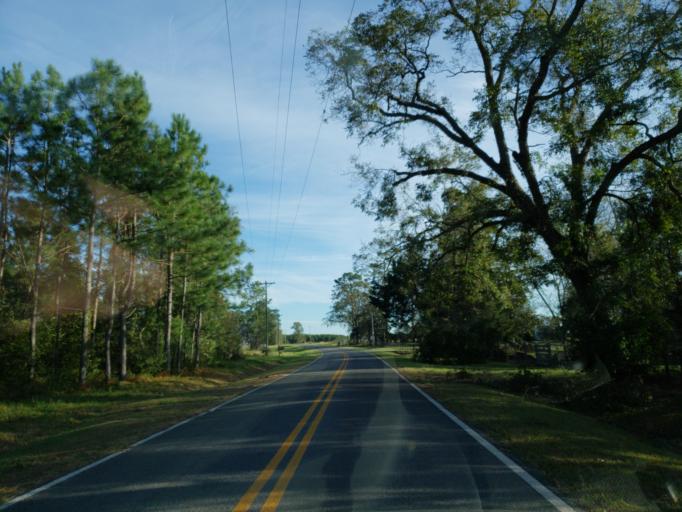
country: US
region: Georgia
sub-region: Dooly County
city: Vienna
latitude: 32.0528
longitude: -83.7614
